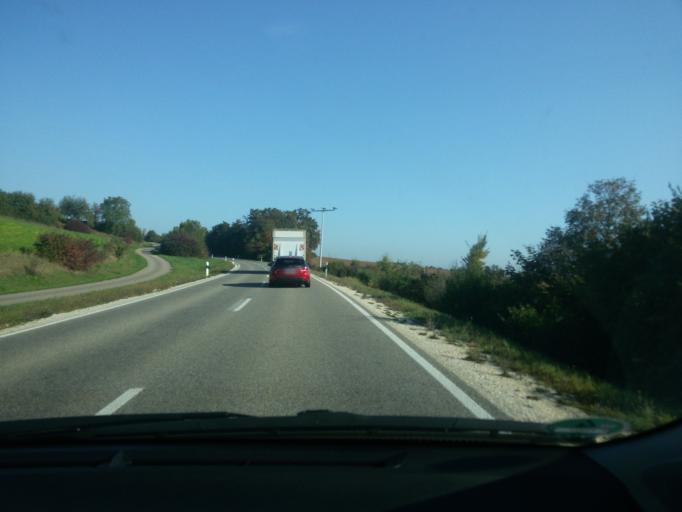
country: DE
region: Bavaria
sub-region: Swabia
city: Alerheim
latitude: 48.8156
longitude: 10.6401
